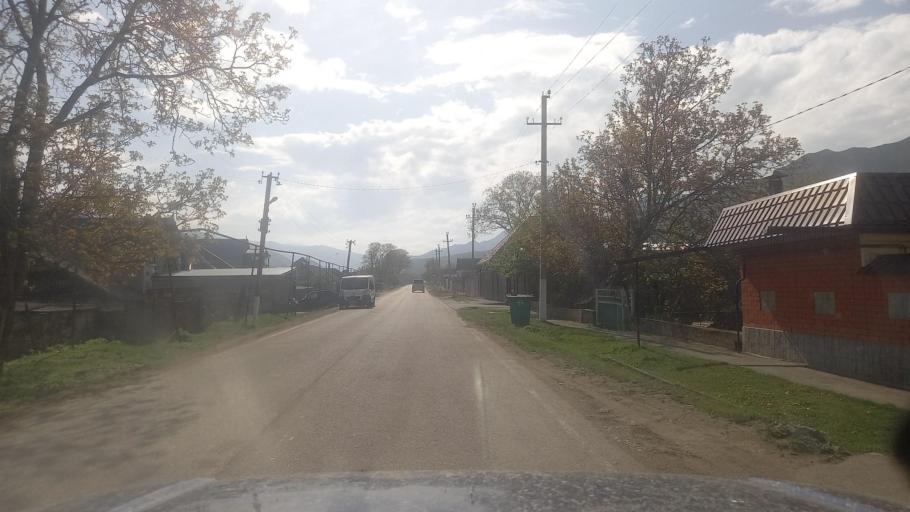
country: RU
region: Kabardino-Balkariya
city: Kamennomostskoye
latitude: 43.7310
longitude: 42.9475
